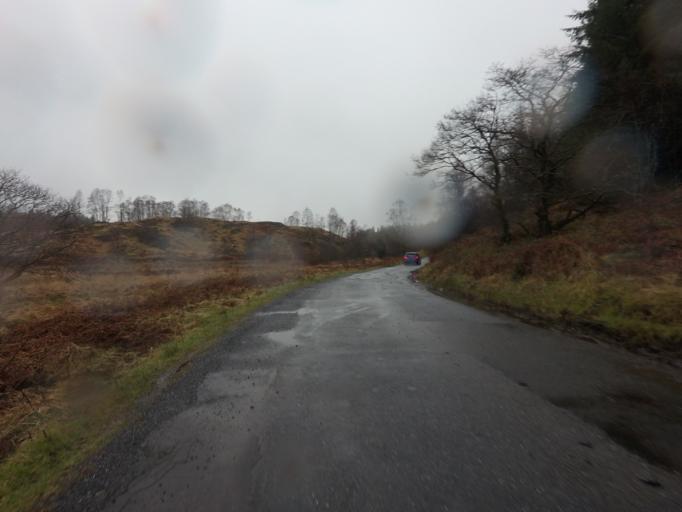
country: GB
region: Scotland
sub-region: West Dunbartonshire
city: Balloch
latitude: 56.2019
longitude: -4.5291
